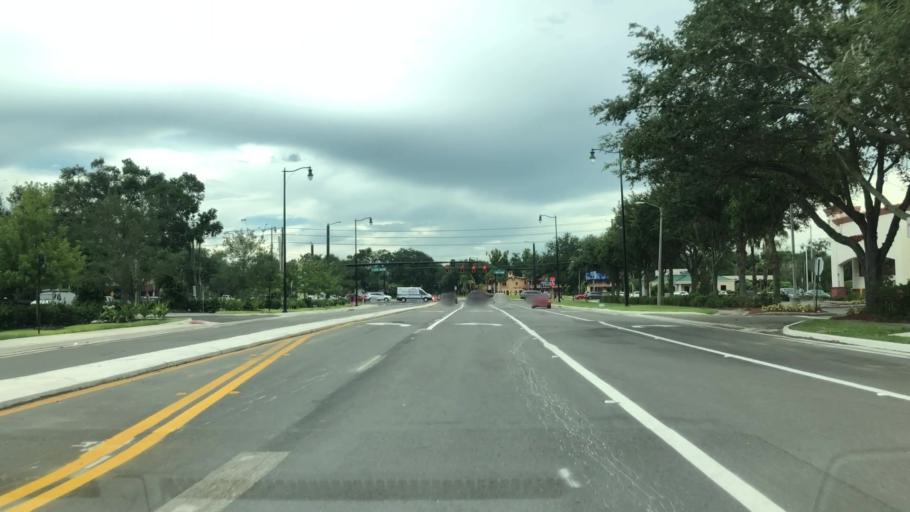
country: US
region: Florida
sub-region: Seminole County
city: Altamonte Springs
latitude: 28.6633
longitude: -81.3936
